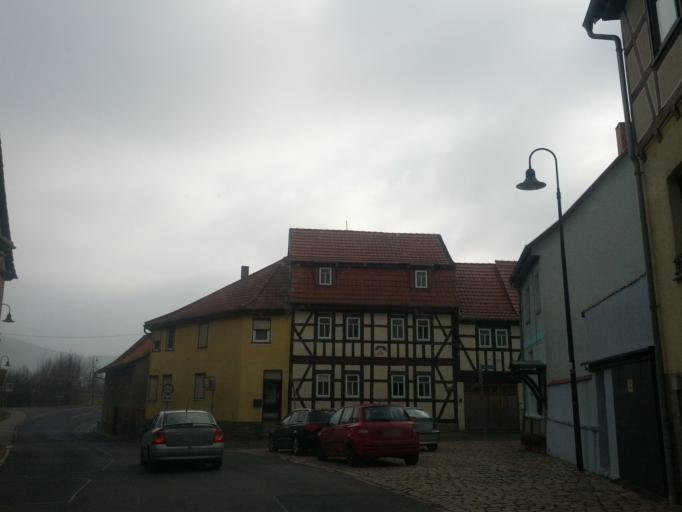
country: DE
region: Thuringia
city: Creuzburg
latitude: 51.0510
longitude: 10.2478
